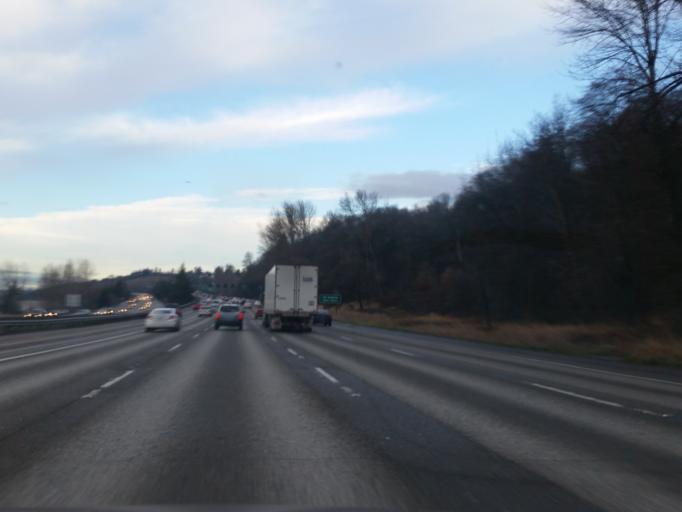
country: US
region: Washington
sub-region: King County
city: Riverton
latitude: 47.5238
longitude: -122.2910
